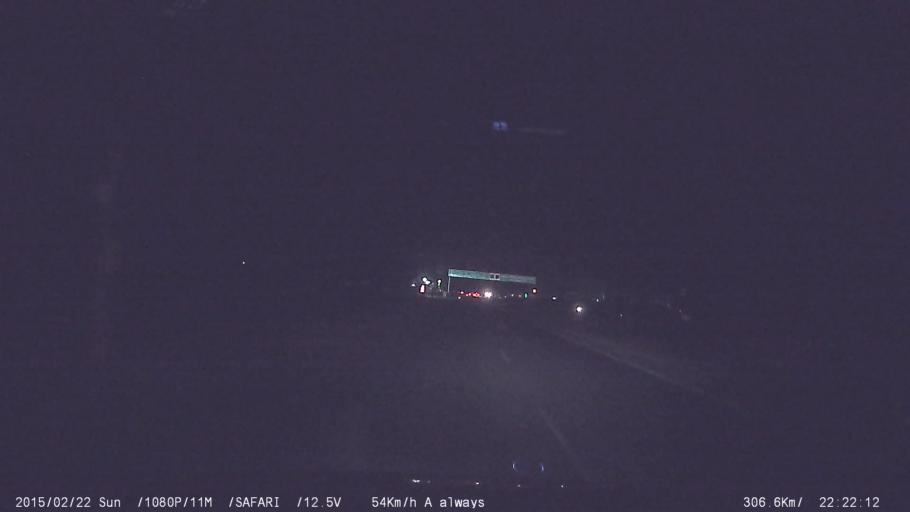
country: IN
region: Tamil Nadu
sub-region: Karur
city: Karur
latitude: 11.0117
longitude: 78.0684
